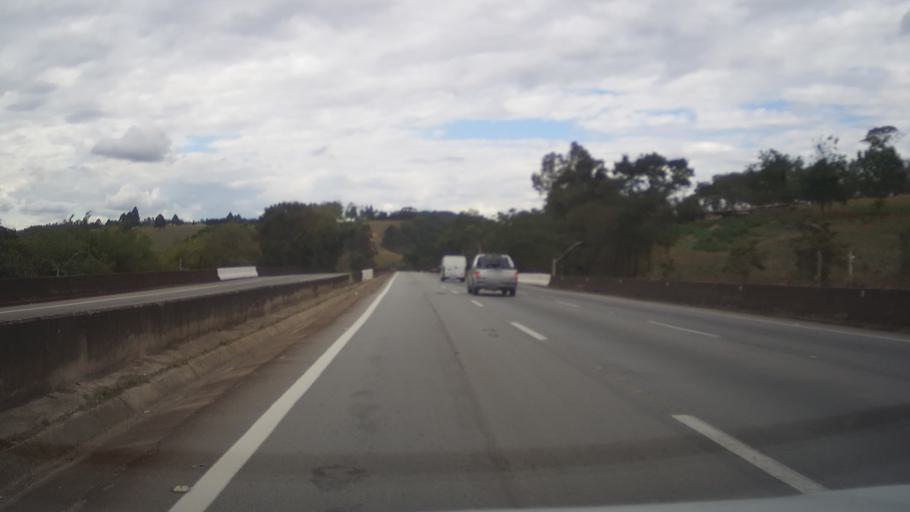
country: BR
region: Minas Gerais
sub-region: Itauna
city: Itauna
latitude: -20.3439
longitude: -44.4410
